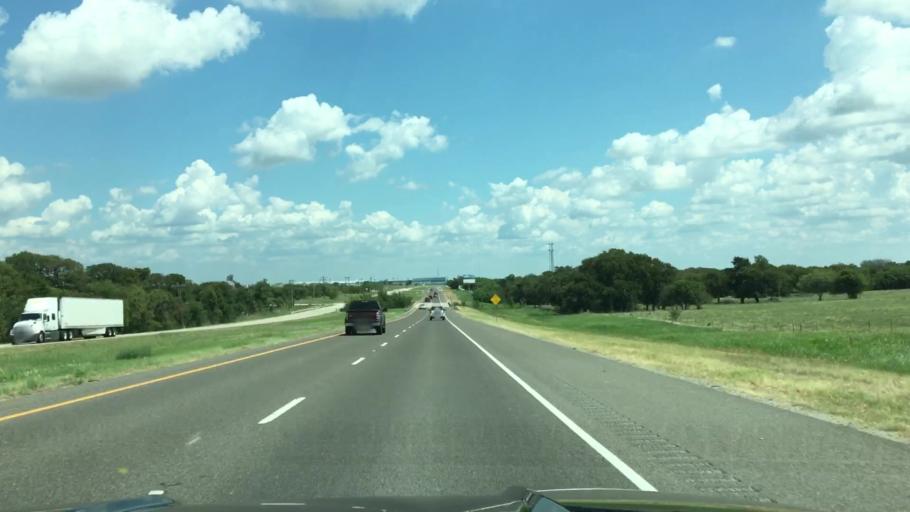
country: US
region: Texas
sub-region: Wise County
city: Rhome
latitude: 33.0366
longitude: -97.4081
